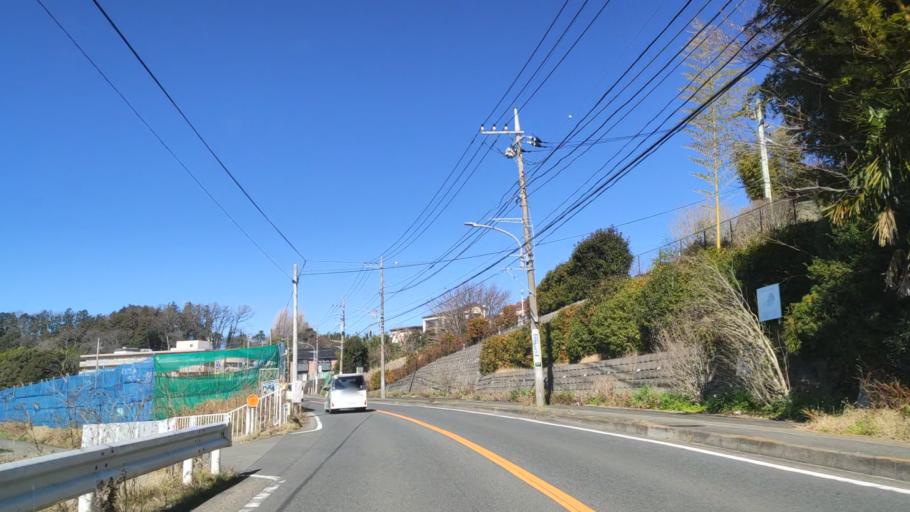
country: JP
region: Tokyo
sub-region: Machida-shi
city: Machida
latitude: 35.5248
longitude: 139.5333
